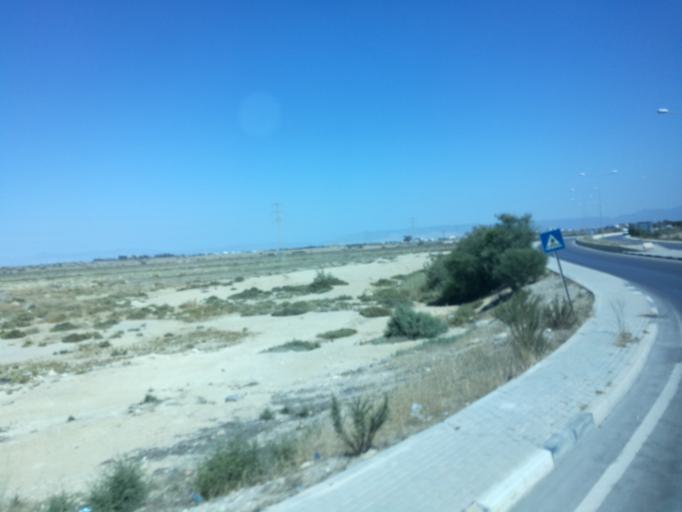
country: CY
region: Ammochostos
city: Famagusta
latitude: 35.1651
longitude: 33.8995
